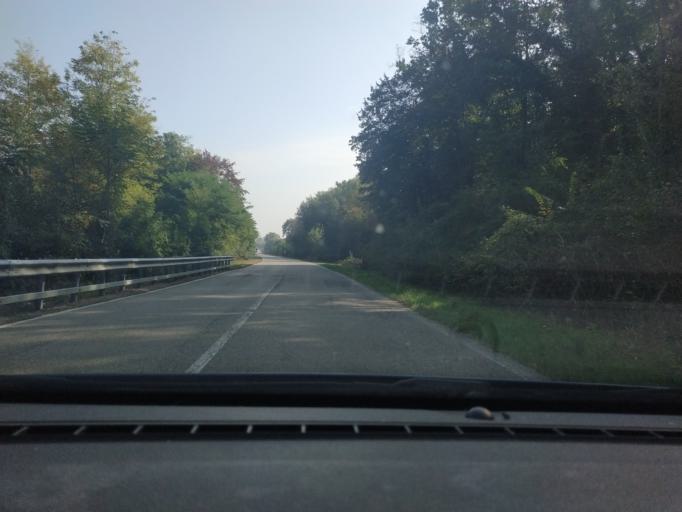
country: IT
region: Piedmont
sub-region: Provincia di Biella
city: Ceresane-Curanuova
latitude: 45.5138
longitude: 7.9924
